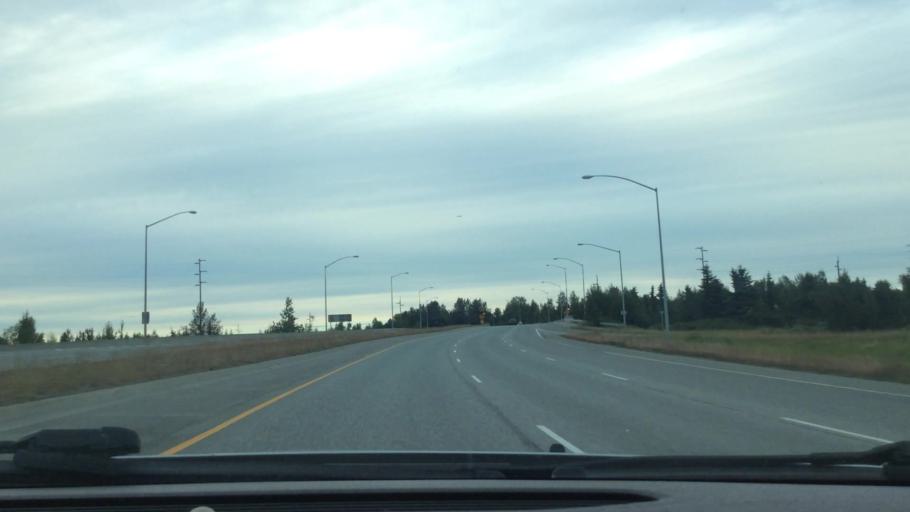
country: US
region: Alaska
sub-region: Anchorage Municipality
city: Anchorage
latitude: 61.1738
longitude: -149.9162
